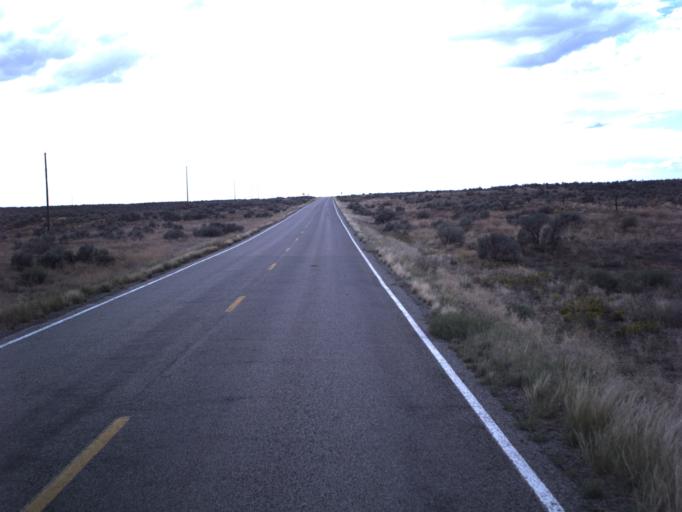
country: US
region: Utah
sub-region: San Juan County
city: Blanding
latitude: 37.4273
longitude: -109.3533
